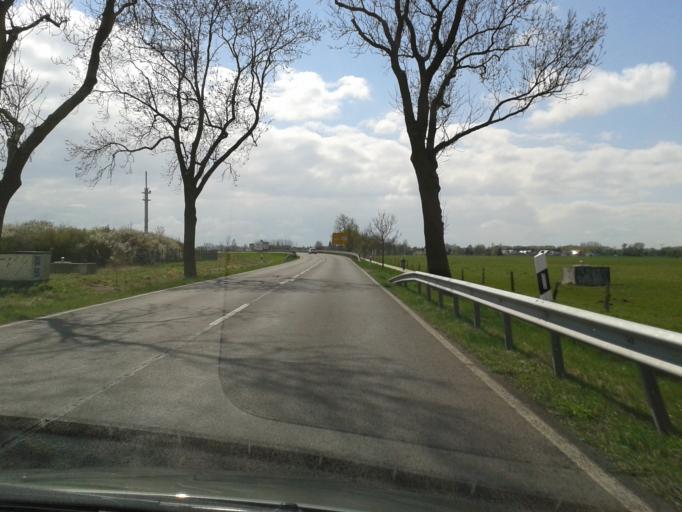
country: DE
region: Saxony-Anhalt
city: Salzwedel
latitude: 52.8747
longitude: 11.1648
